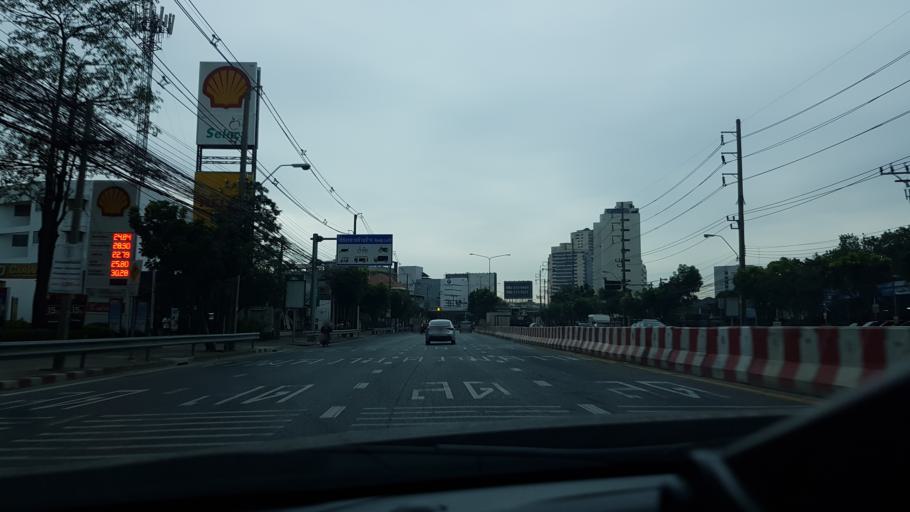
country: TH
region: Bangkok
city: Chatuchak
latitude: 13.8234
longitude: 100.5738
